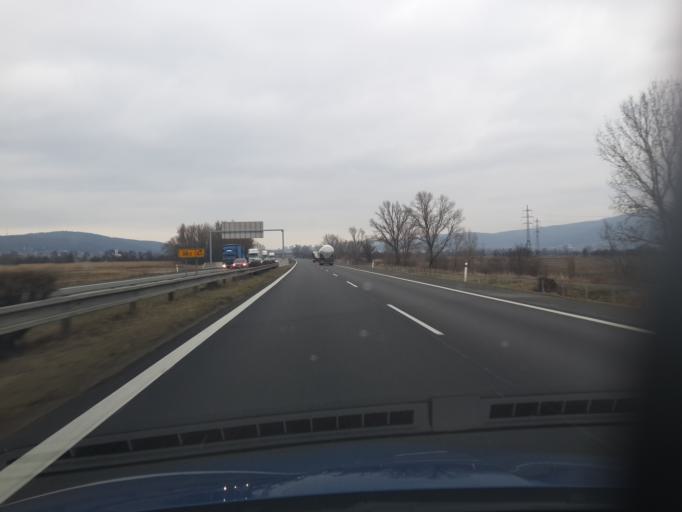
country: SK
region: Bratislavsky
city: Stupava
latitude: 48.2421
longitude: 17.0156
